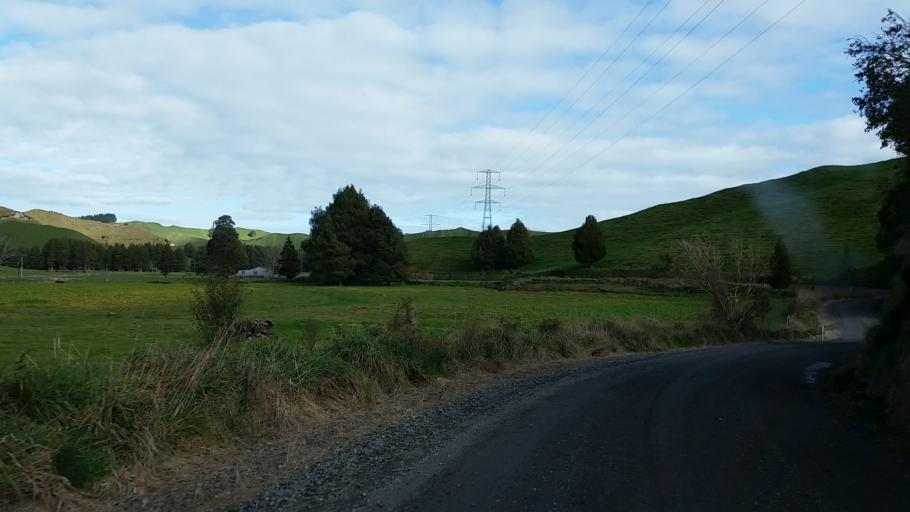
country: NZ
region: Taranaki
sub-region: South Taranaki District
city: Eltham
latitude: -39.2551
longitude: 174.5213
